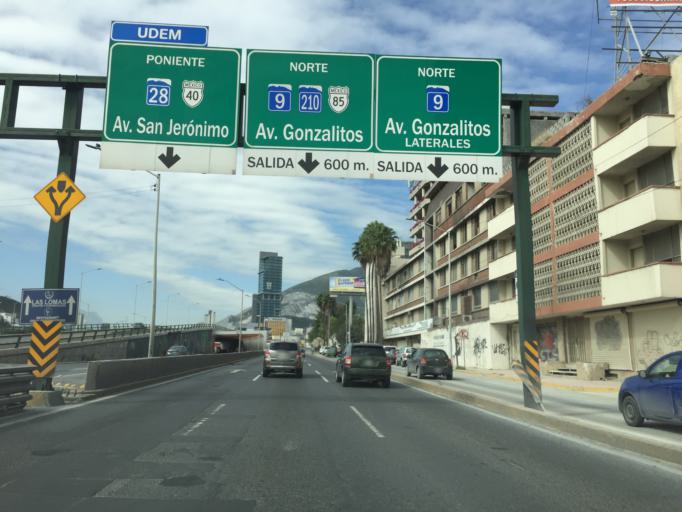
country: MX
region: Nuevo Leon
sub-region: Monterrey
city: Monterrey
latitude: 25.6712
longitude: -100.3477
